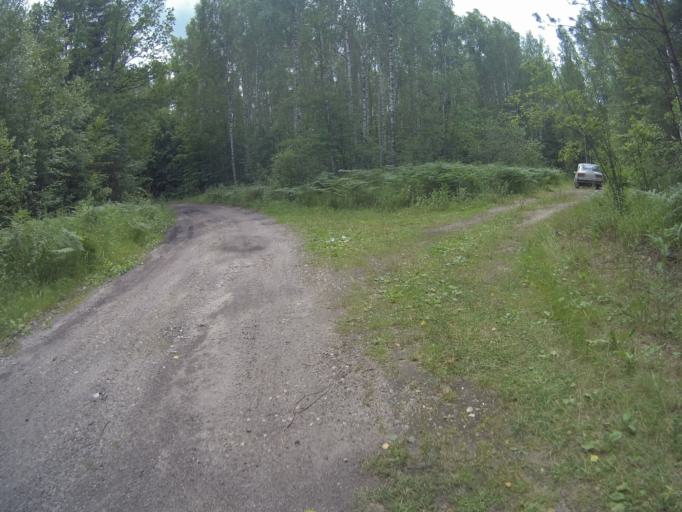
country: RU
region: Vladimir
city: Raduzhnyy
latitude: 56.0569
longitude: 40.3084
